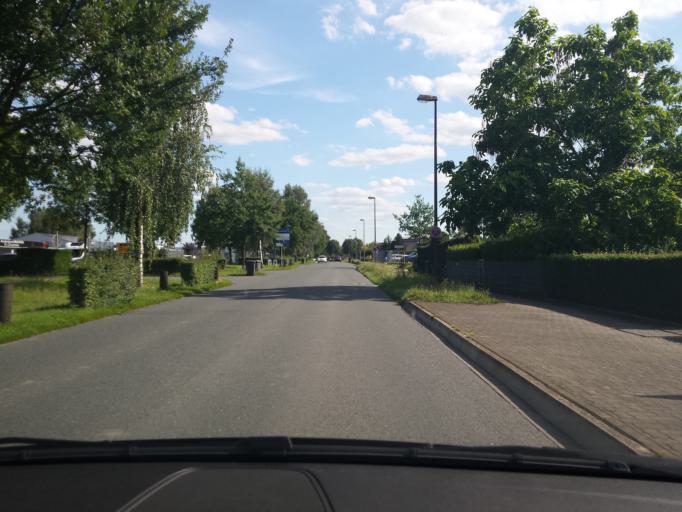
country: DE
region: North Rhine-Westphalia
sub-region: Regierungsbezirk Arnsberg
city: Lippstadt
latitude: 51.6557
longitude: 8.3559
